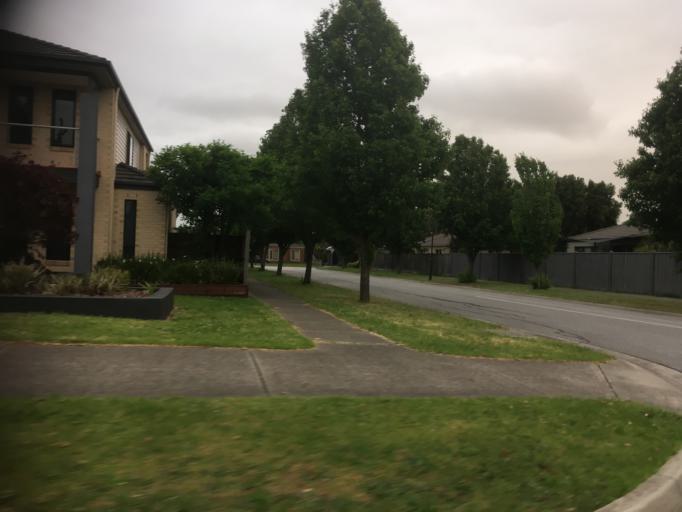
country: AU
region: Victoria
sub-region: Casey
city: Narre Warren South
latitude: -38.0707
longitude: 145.3172
